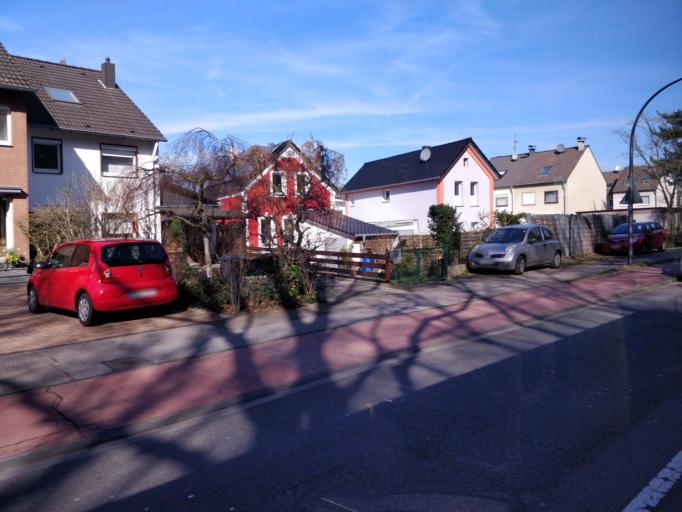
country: DE
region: North Rhine-Westphalia
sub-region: Regierungsbezirk Koln
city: Wahn-Heide
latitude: 50.8525
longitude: 7.1090
